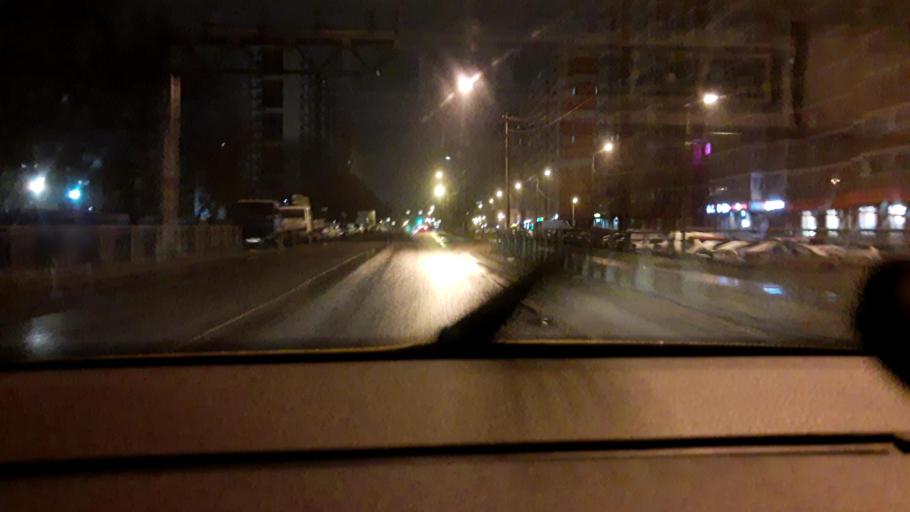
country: RU
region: Moskovskaya
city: Shchelkovo
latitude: 55.9353
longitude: 37.9771
